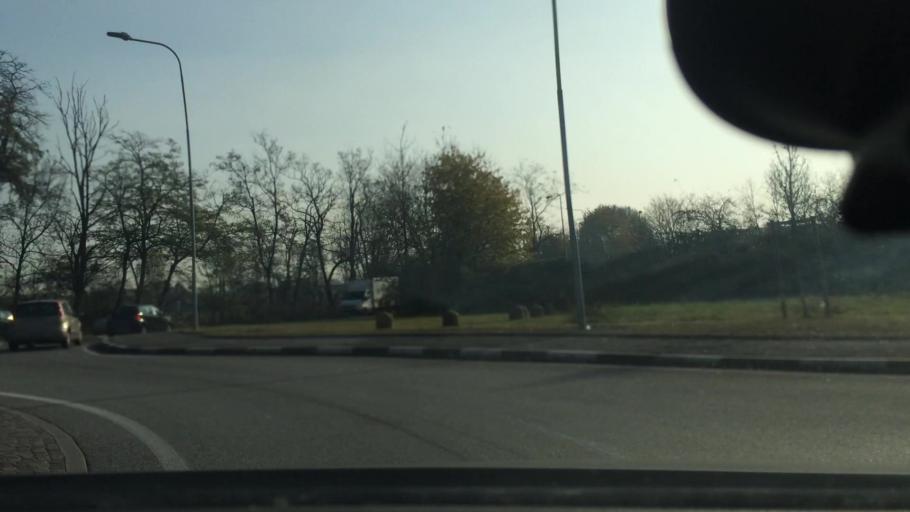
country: IT
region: Lombardy
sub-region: Citta metropolitana di Milano
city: Passirana
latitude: 45.5575
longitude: 9.0522
